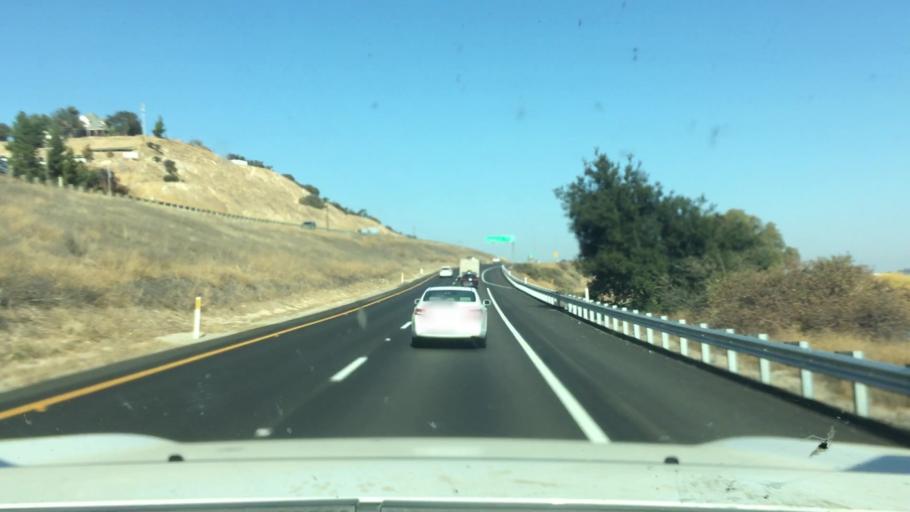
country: US
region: California
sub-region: San Luis Obispo County
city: Paso Robles
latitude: 35.6049
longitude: -120.6923
